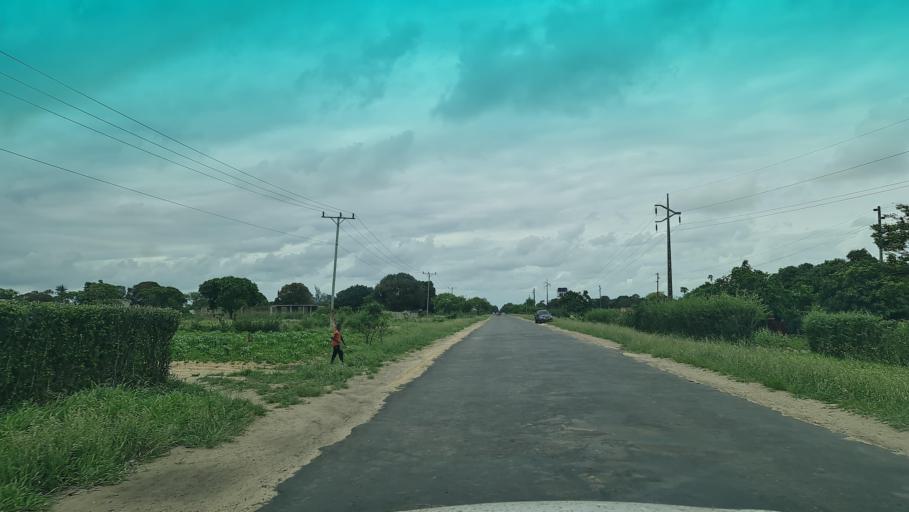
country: MZ
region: Maputo
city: Manhica
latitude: -25.4290
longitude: 32.7728
